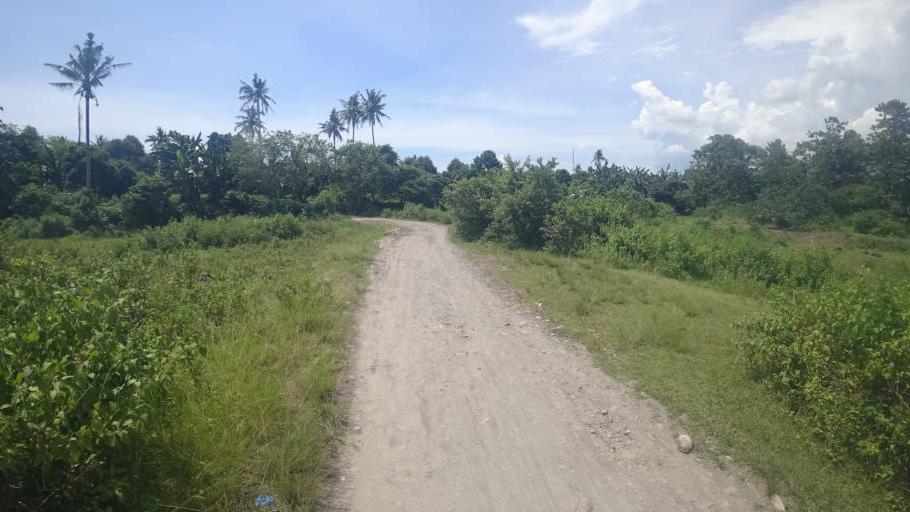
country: PH
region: Eastern Visayas
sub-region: Province of Leyte
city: Jaro
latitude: 11.2006
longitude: 124.8078
